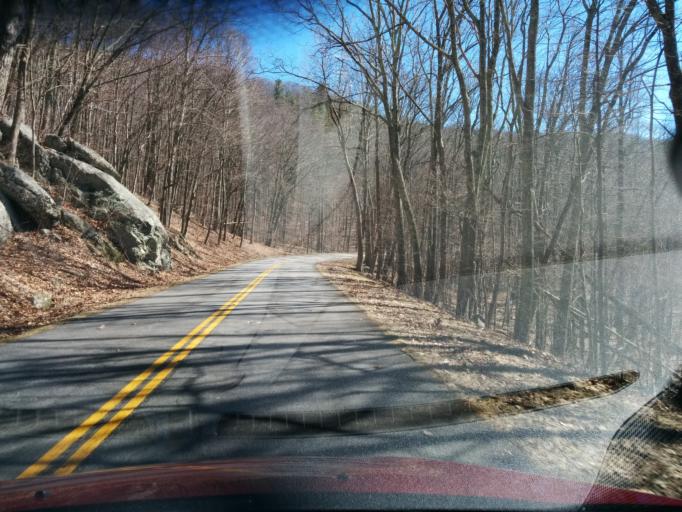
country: US
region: Virginia
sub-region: City of Buena Vista
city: Buena Vista
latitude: 37.8188
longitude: -79.1760
